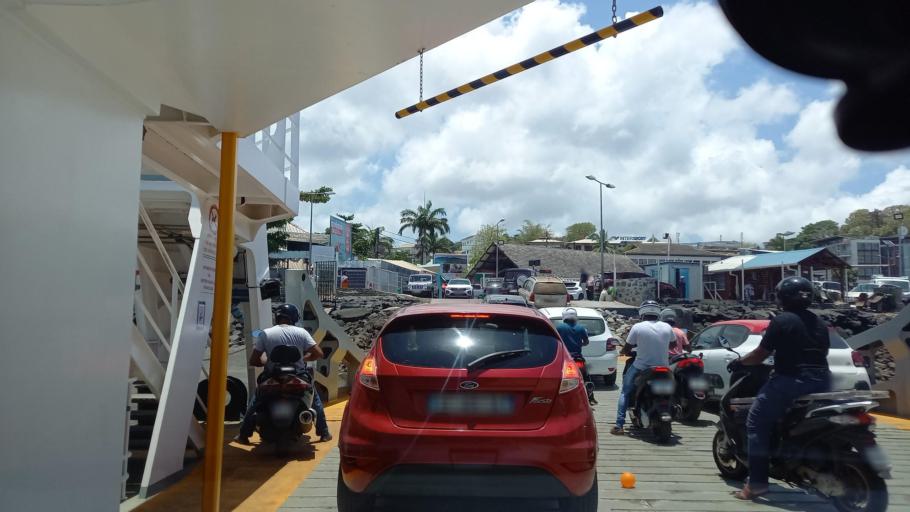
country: YT
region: Mamoudzou
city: Mamoudzou
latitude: -12.7783
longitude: 45.2329
